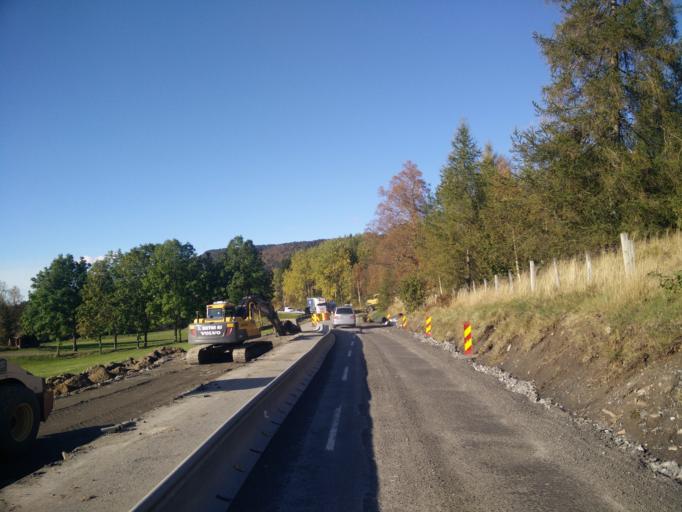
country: NO
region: More og Romsdal
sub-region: Halsa
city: Liaboen
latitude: 63.1121
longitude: 8.3262
